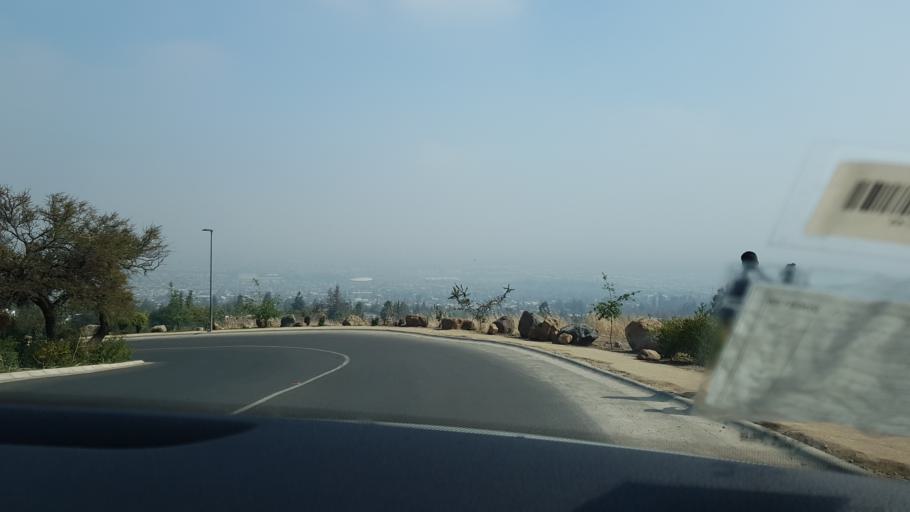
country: CL
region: Santiago Metropolitan
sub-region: Provincia de Santiago
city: Villa Presidente Frei, Nunoa, Santiago, Chile
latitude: -33.4763
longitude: -70.5152
